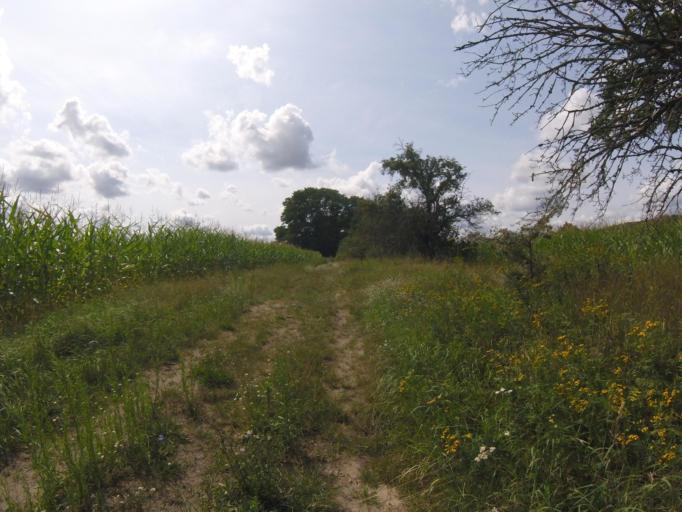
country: DE
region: Brandenburg
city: Mittenwalde
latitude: 52.2917
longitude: 13.5078
